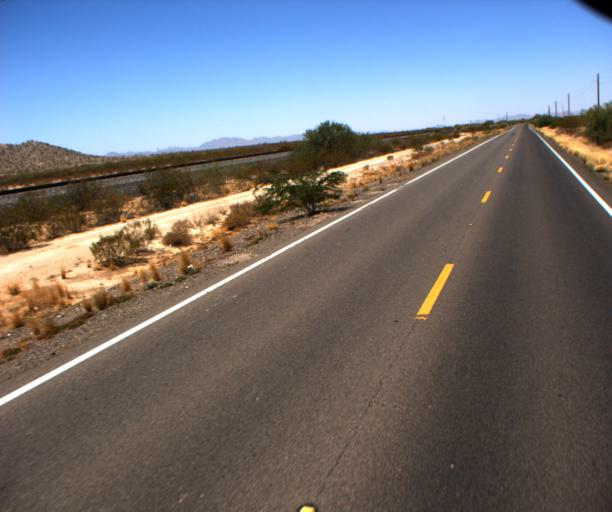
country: US
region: Arizona
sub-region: Pinal County
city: Maricopa
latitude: 33.0742
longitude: -112.1799
